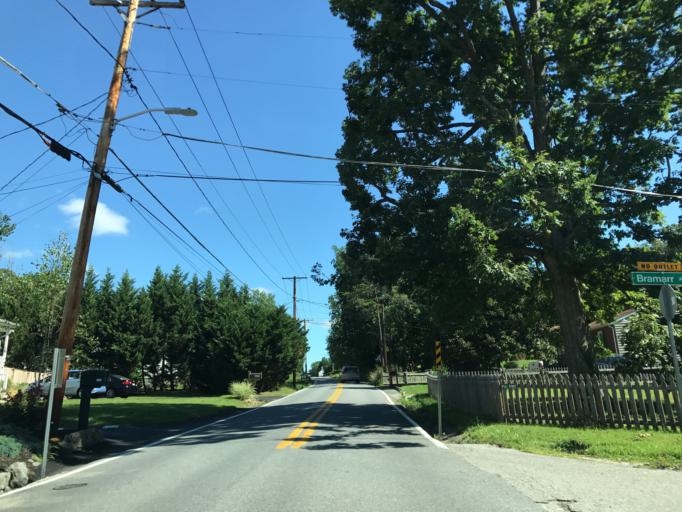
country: US
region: Maryland
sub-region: Howard County
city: Ellicott City
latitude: 39.2775
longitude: -76.7775
